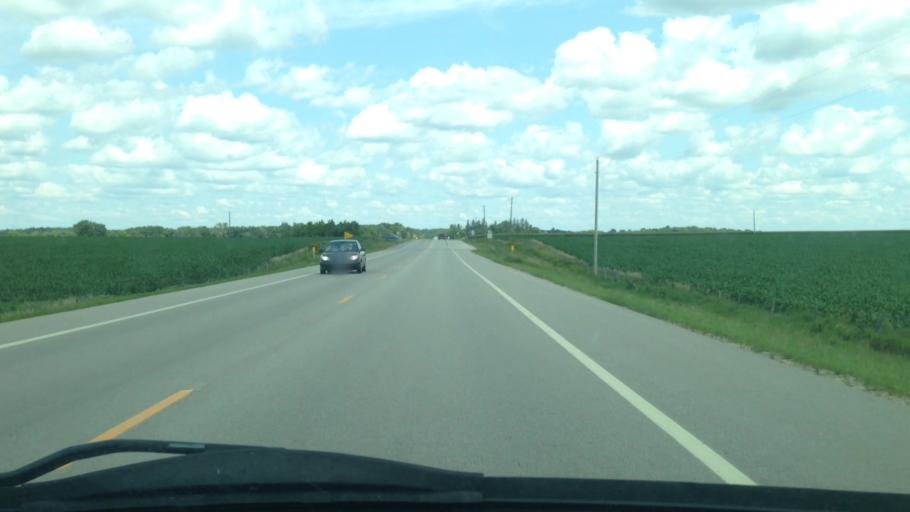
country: US
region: Minnesota
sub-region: Olmsted County
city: Rochester
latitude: 43.9614
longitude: -92.5183
